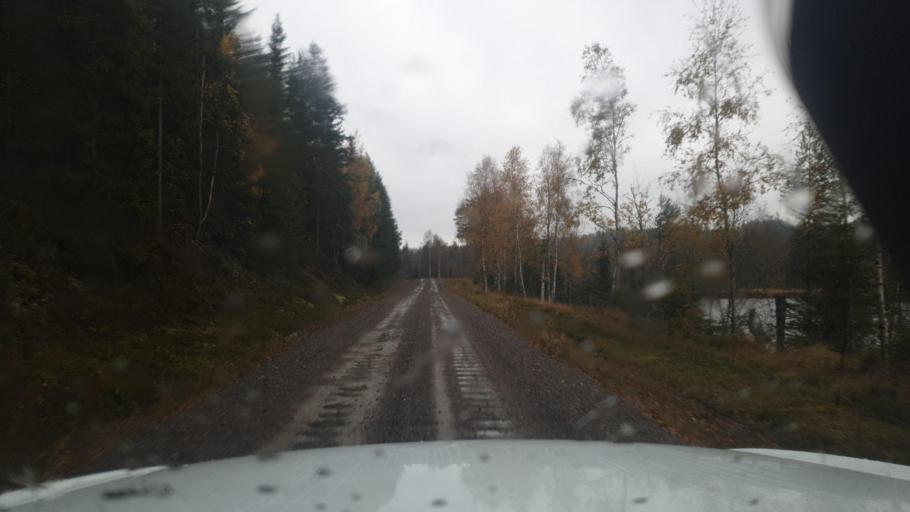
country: SE
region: Vaermland
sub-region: Eda Kommun
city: Charlottenberg
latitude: 60.1062
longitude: 12.6062
